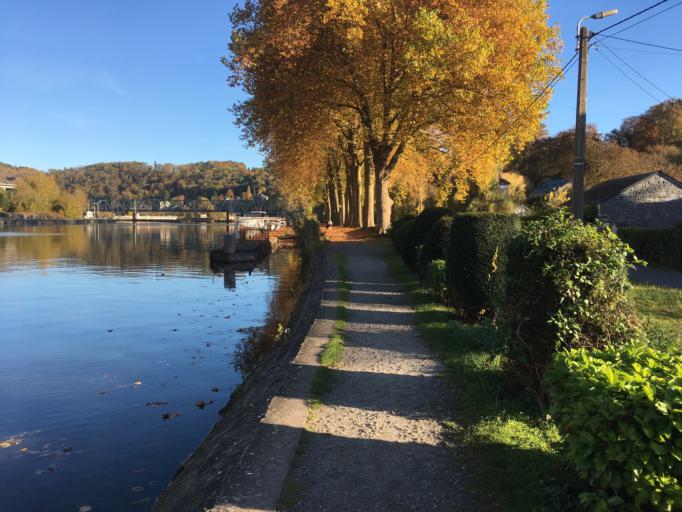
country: BE
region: Wallonia
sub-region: Province de Namur
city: Dinant
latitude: 50.2407
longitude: 4.9008
